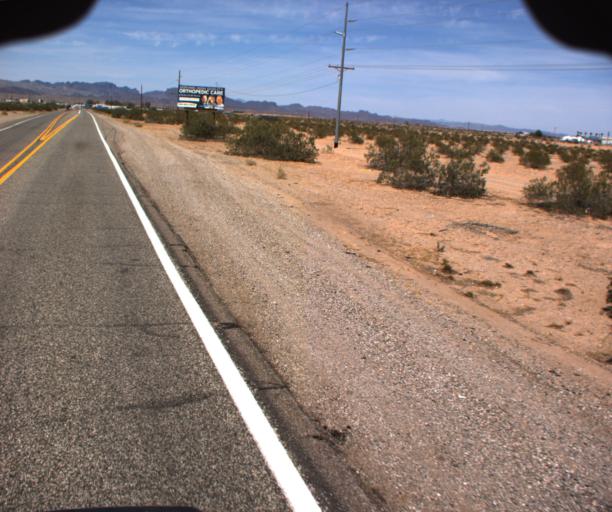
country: US
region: Arizona
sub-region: La Paz County
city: Parker
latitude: 34.1259
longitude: -114.2794
